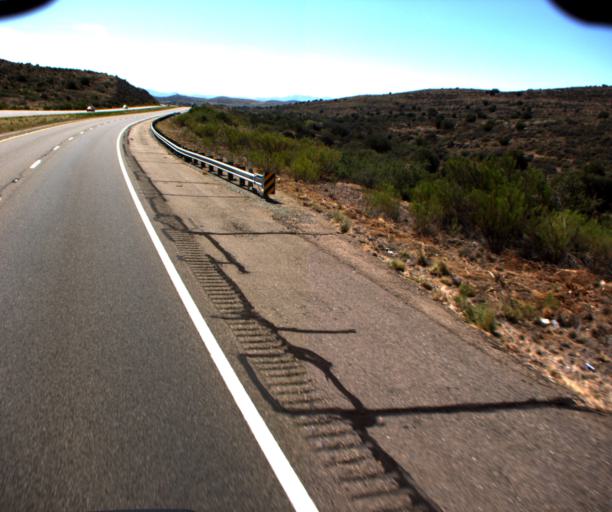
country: US
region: Arizona
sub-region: Yavapai County
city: Spring Valley
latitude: 34.3691
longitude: -112.1809
